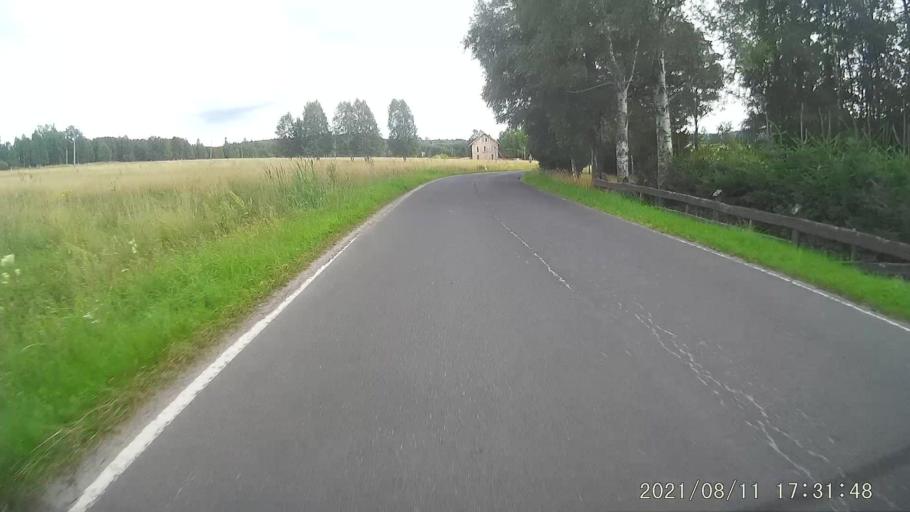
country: PL
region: Lower Silesian Voivodeship
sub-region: Powiat klodzki
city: Szczytna
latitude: 50.3037
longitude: 16.4537
